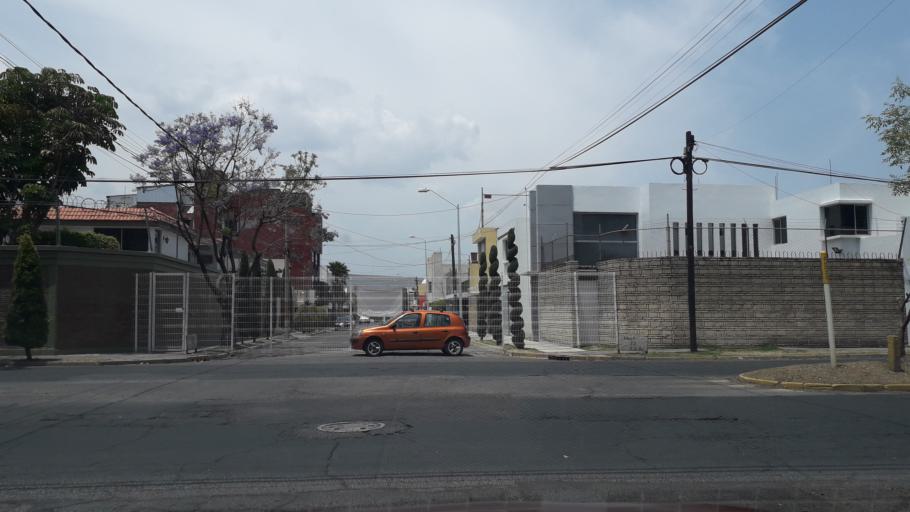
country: MX
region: Puebla
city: Puebla
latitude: 19.0197
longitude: -98.1940
